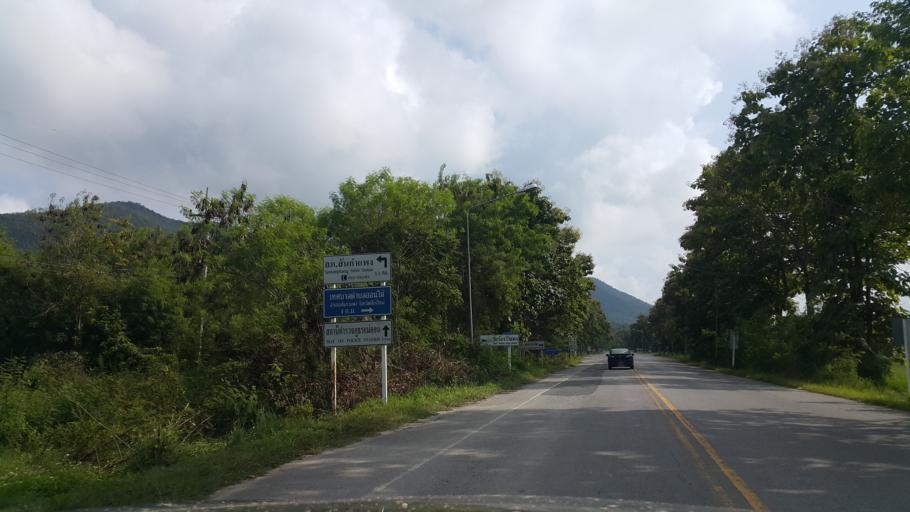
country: TH
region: Chiang Mai
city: Mae On
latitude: 18.7407
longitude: 99.2021
